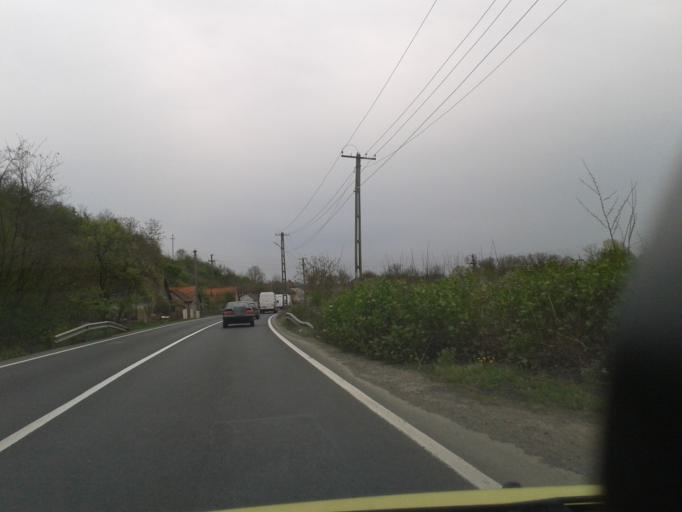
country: RO
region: Arad
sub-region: Comuna Bata
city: Bata
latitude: 46.0538
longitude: 22.0491
